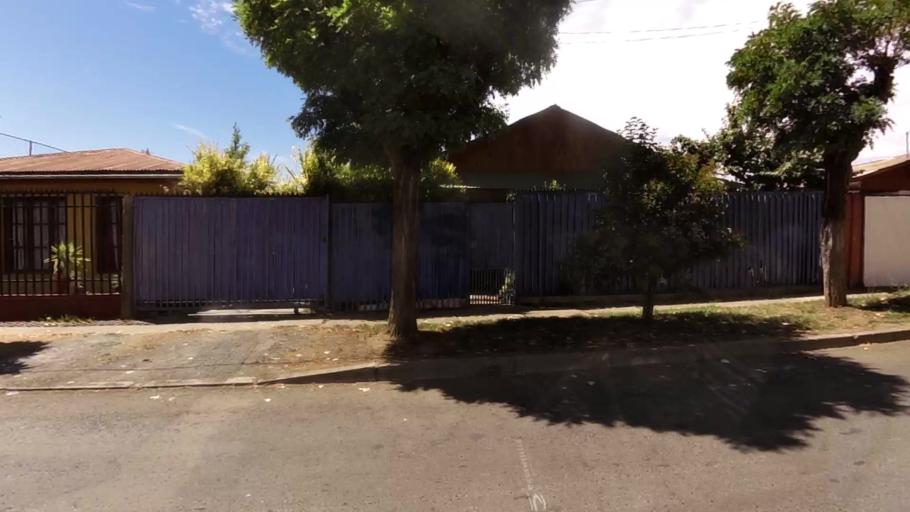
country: CL
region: O'Higgins
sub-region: Provincia de Cachapoal
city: Graneros
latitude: -33.9841
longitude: -70.7083
